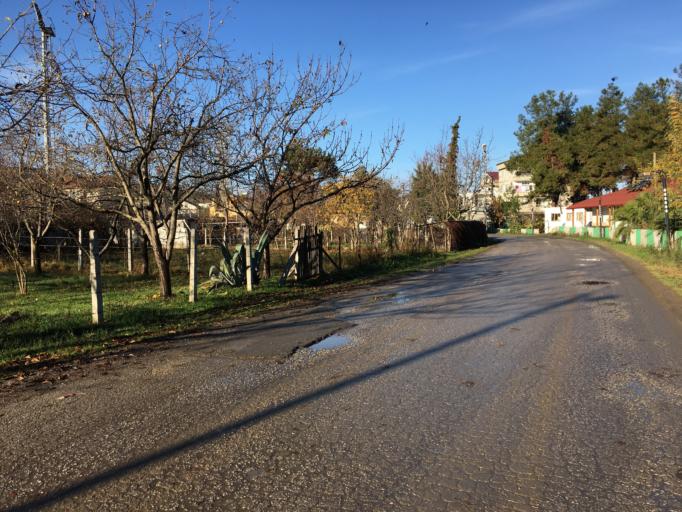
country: TR
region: Samsun
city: Alacam
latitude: 41.6133
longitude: 35.6035
